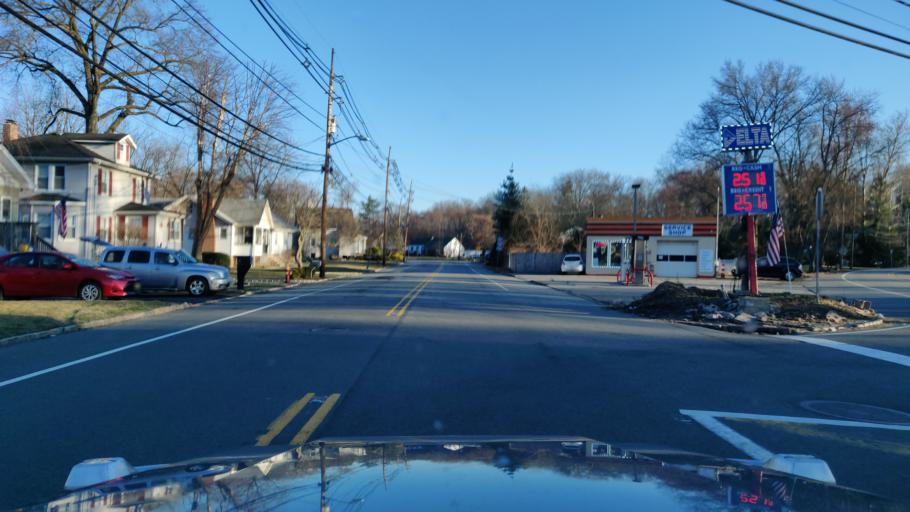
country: US
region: New Jersey
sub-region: Essex County
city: Westville
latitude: 40.8604
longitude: -74.3130
